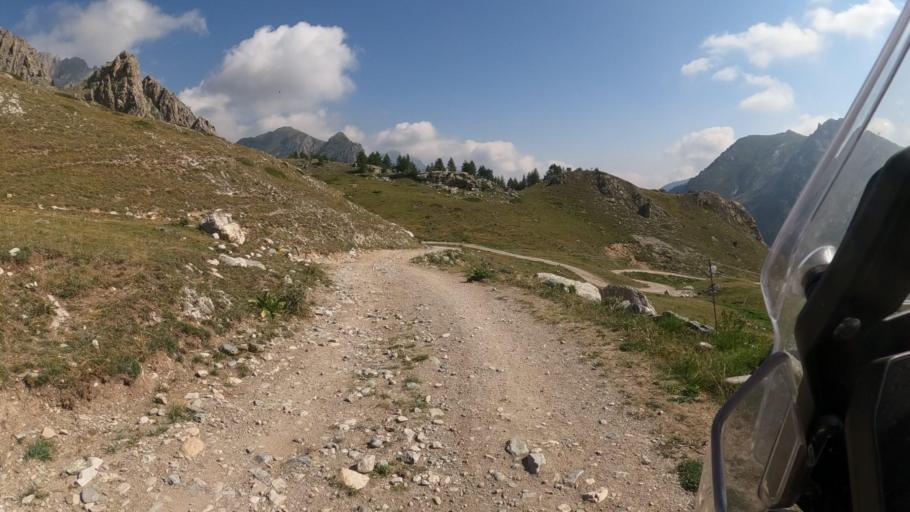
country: IT
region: Piedmont
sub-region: Provincia di Cuneo
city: Pietraporzio
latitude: 44.4029
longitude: 7.0379
